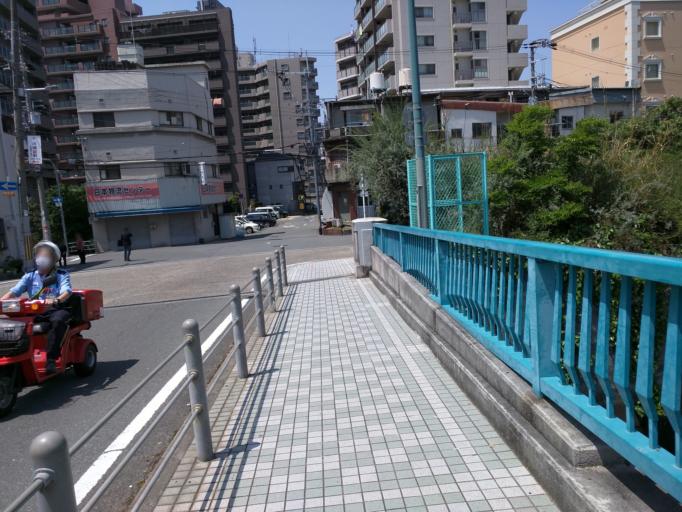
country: JP
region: Osaka
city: Osaka-shi
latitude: 34.6793
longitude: 135.4822
